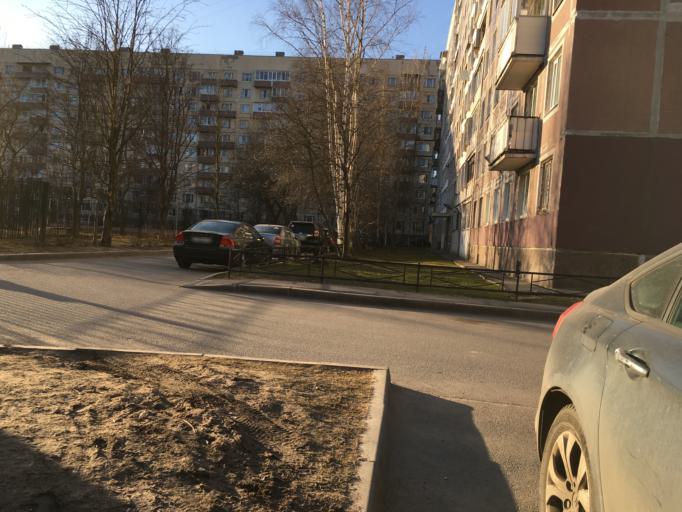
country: RU
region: St.-Petersburg
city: Staraya Derevnya
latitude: 60.0142
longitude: 30.2461
